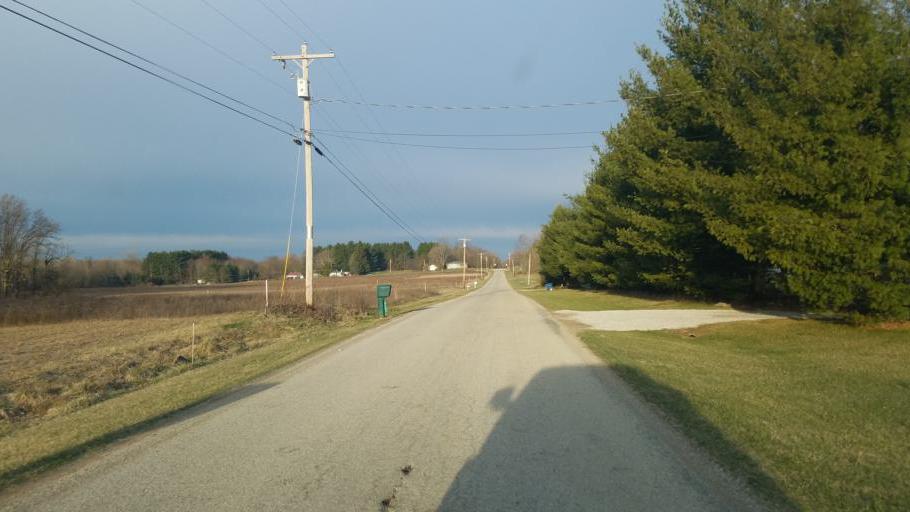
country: US
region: Ohio
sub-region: Knox County
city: Centerburg
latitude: 40.3909
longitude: -82.7554
